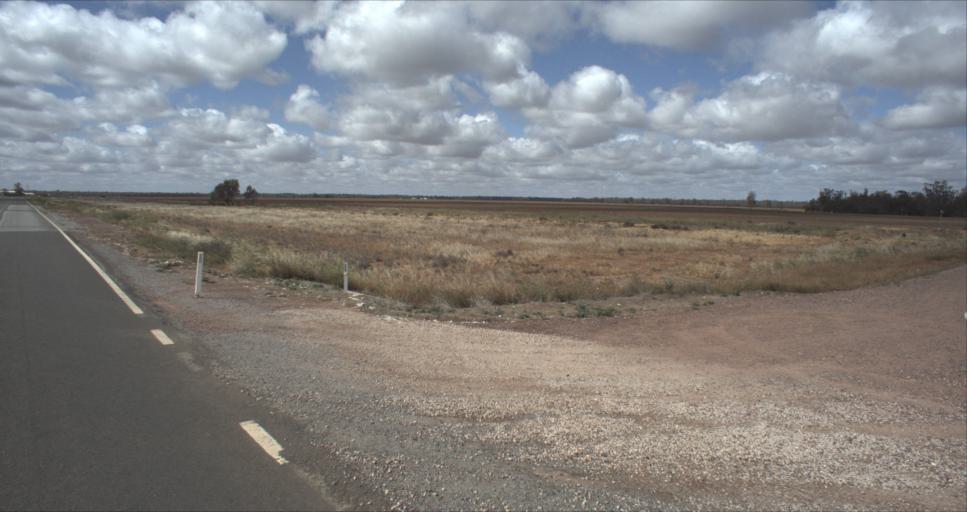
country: AU
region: New South Wales
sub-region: Murrumbidgee Shire
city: Darlington Point
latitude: -34.5807
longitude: 146.1107
